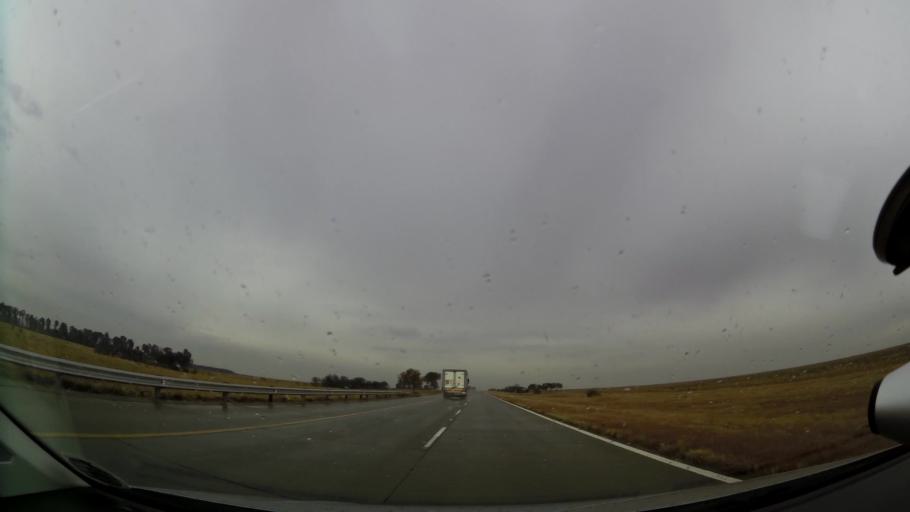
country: ZA
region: Gauteng
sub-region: Sedibeng District Municipality
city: Vanderbijlpark
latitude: -26.6510
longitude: 27.7412
